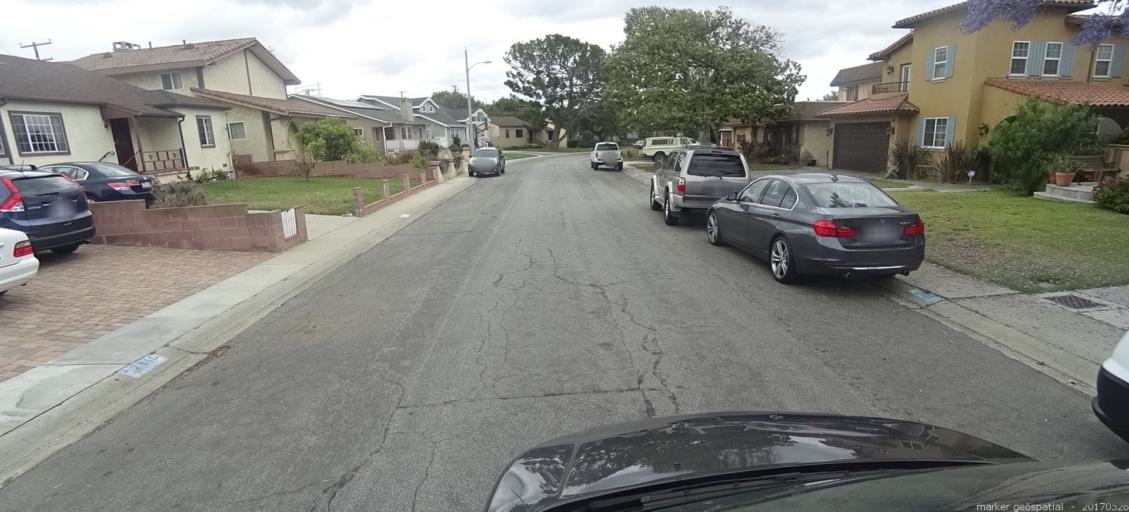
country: US
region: California
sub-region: Los Angeles County
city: Lawndale
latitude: 33.8814
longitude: -118.3685
